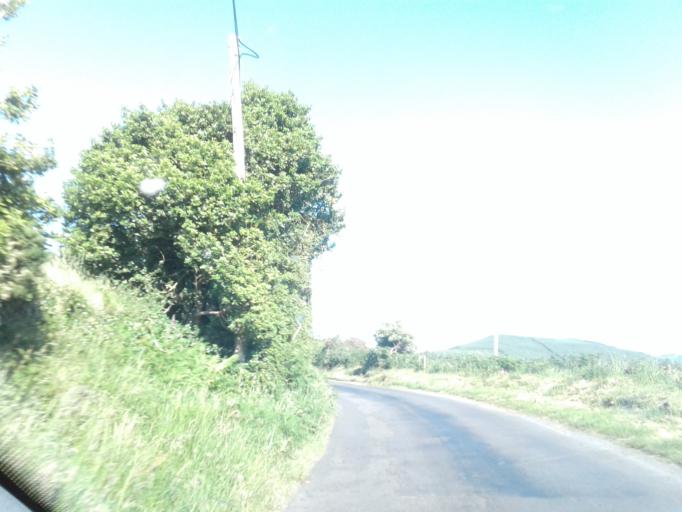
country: IE
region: Leinster
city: Ballinteer
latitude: 53.1903
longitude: -6.2578
